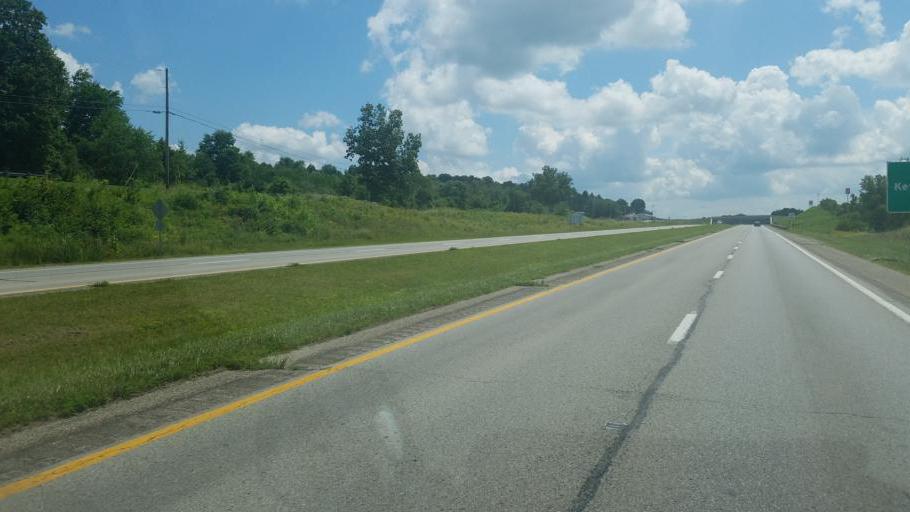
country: US
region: Ohio
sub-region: Jackson County
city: Jackson
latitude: 39.0407
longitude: -82.6071
